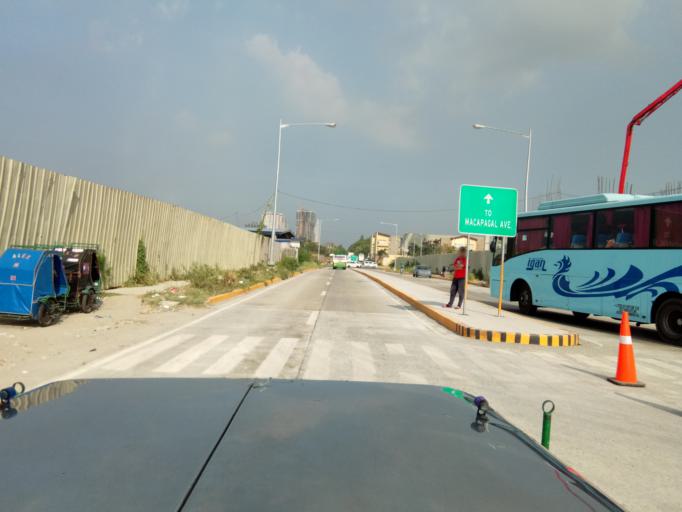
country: PH
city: Sambayanihan People's Village
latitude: 14.5075
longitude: 120.9900
